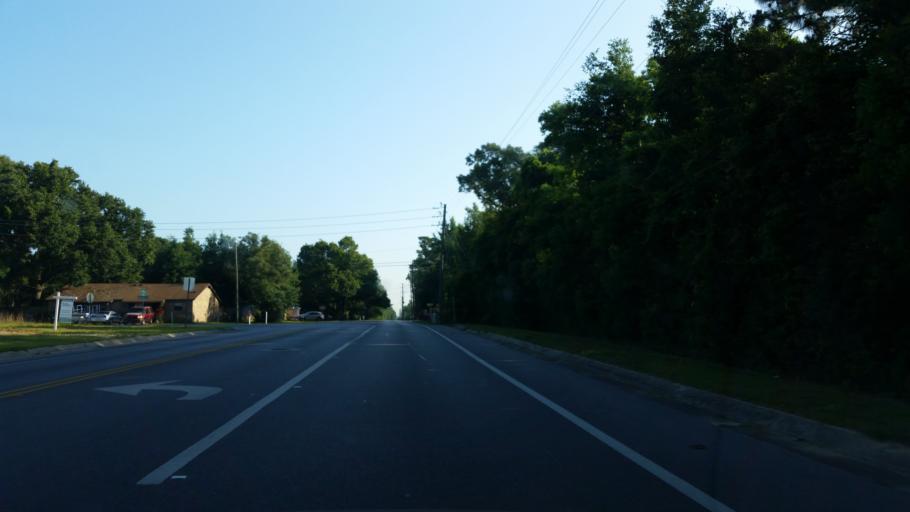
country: US
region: Florida
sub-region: Escambia County
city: Ferry Pass
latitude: 30.5166
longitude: -87.2377
